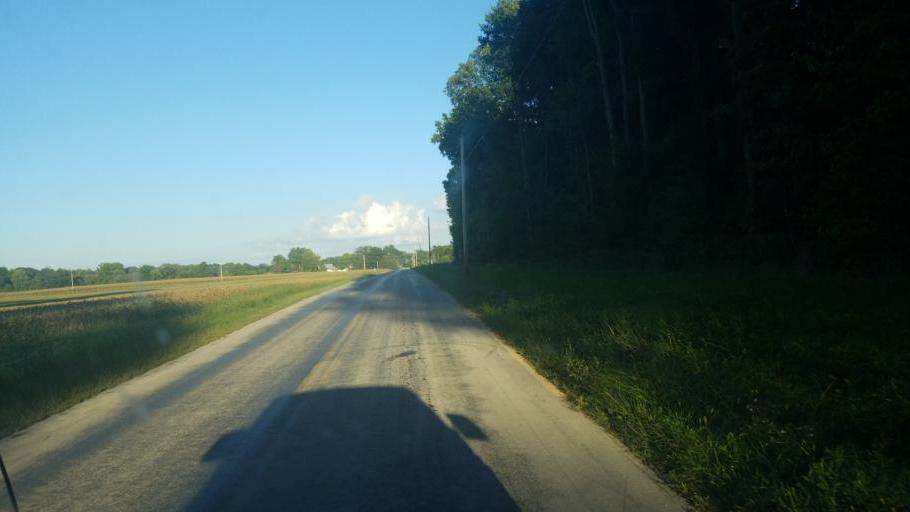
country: US
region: Ohio
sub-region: Wyandot County
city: Upper Sandusky
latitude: 40.8765
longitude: -83.2269
